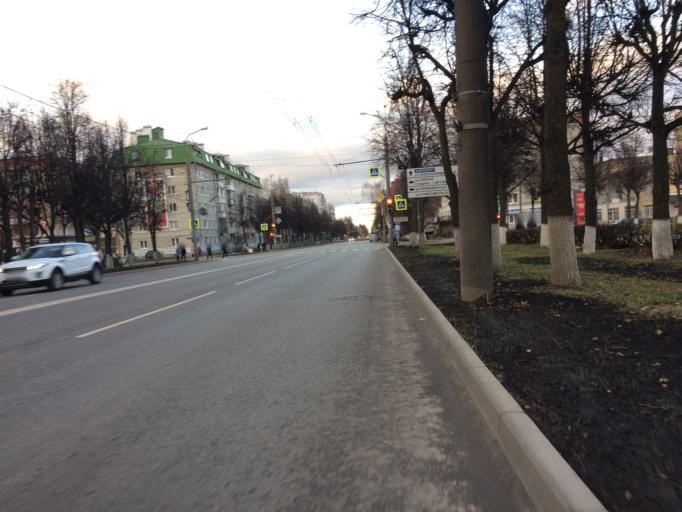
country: RU
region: Mariy-El
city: Yoshkar-Ola
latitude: 56.6392
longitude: 47.8880
